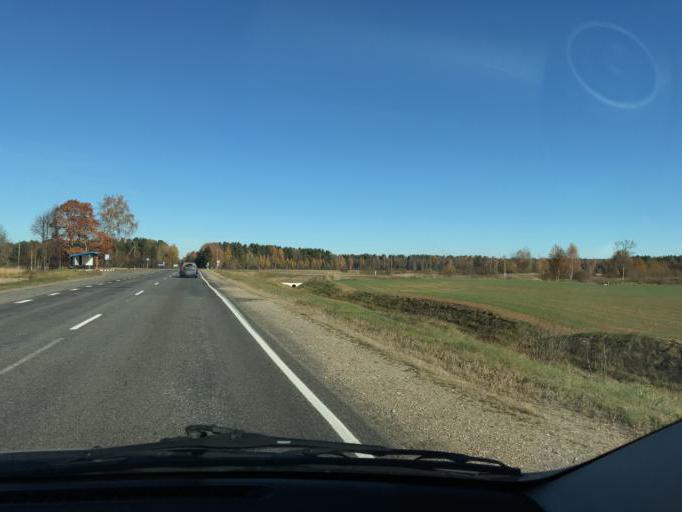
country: BY
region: Vitebsk
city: Lyepyel'
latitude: 55.0554
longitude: 28.7517
